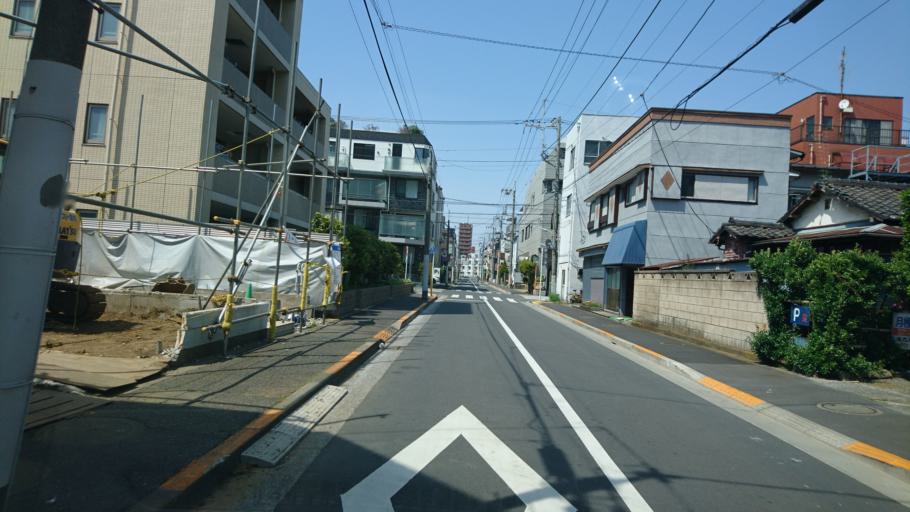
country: JP
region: Kanagawa
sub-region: Kawasaki-shi
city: Kawasaki
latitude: 35.5686
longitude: 139.7060
